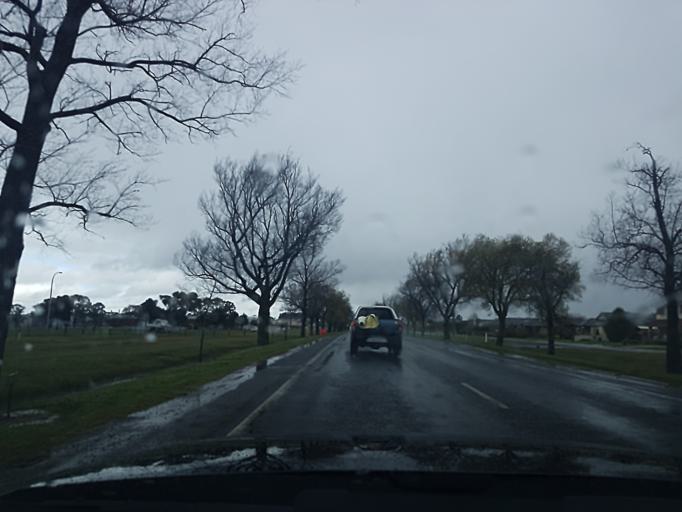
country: AU
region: Victoria
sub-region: Ballarat North
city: Newington
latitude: -37.5437
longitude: 143.7904
